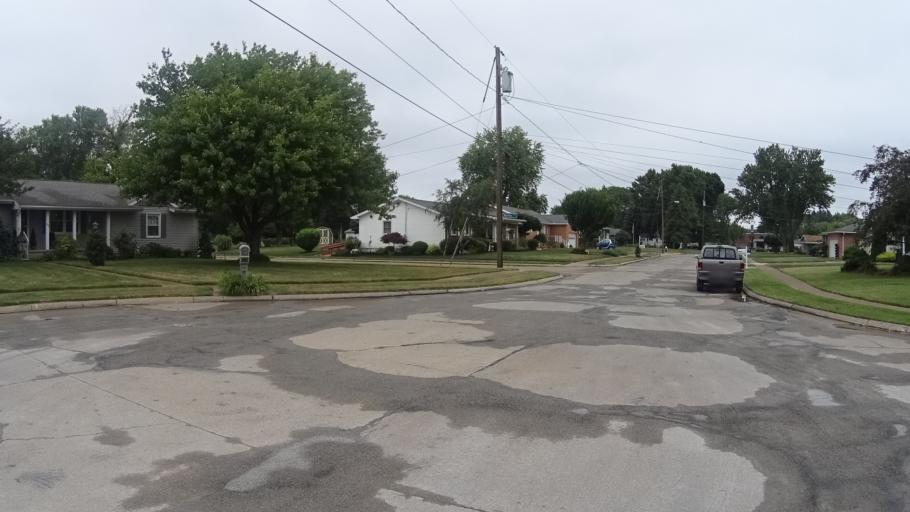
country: US
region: Ohio
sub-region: Erie County
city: Sandusky
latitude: 41.4384
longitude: -82.6776
